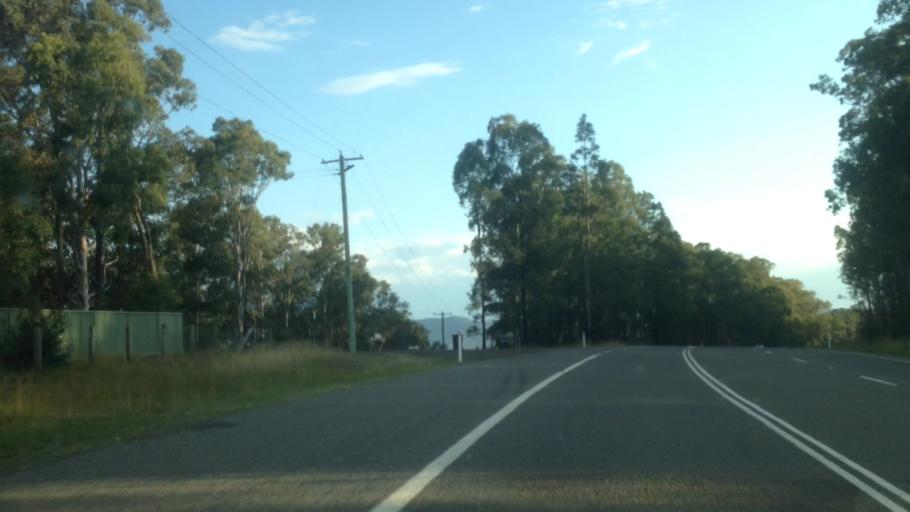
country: AU
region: New South Wales
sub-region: Cessnock
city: Kurri Kurri
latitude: -32.8601
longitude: 151.4839
